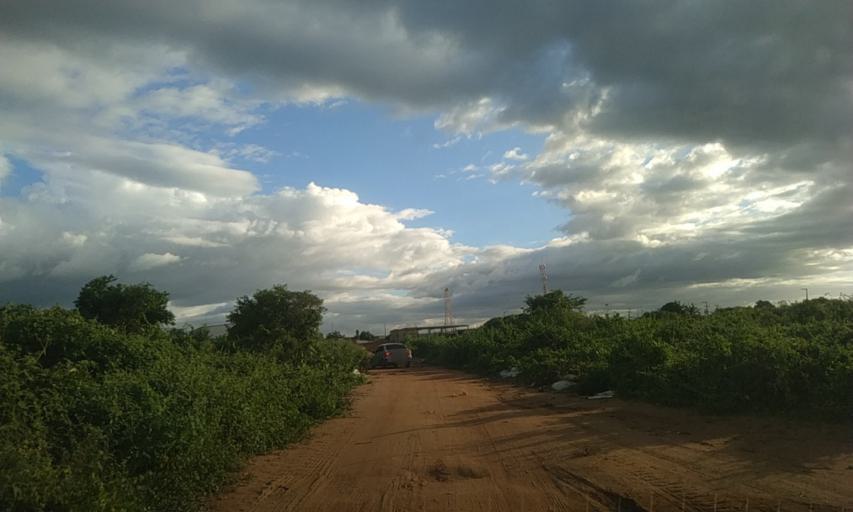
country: BR
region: Rio Grande do Norte
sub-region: Mossoro
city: Mossoro
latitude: -5.2232
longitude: -37.3411
